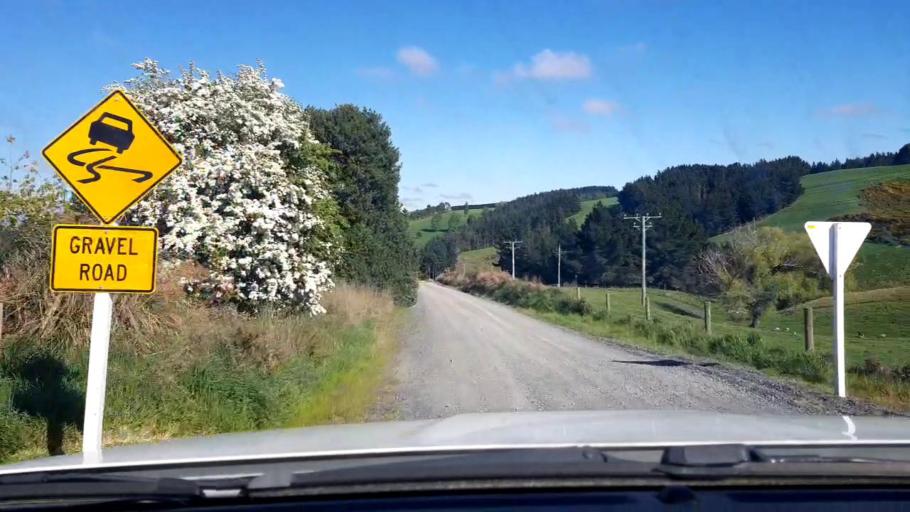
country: NZ
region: Otago
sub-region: Clutha District
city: Balclutha
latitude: -46.2239
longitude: 169.7466
